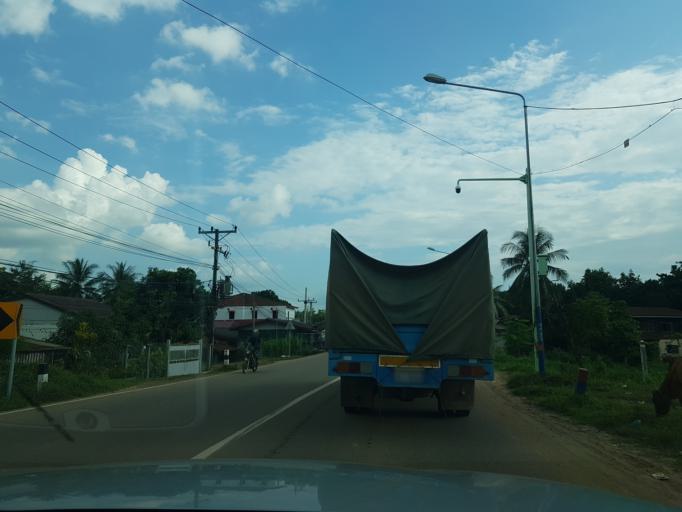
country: TH
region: Nong Khai
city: Si Chiang Mai
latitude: 17.9776
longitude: 102.4963
